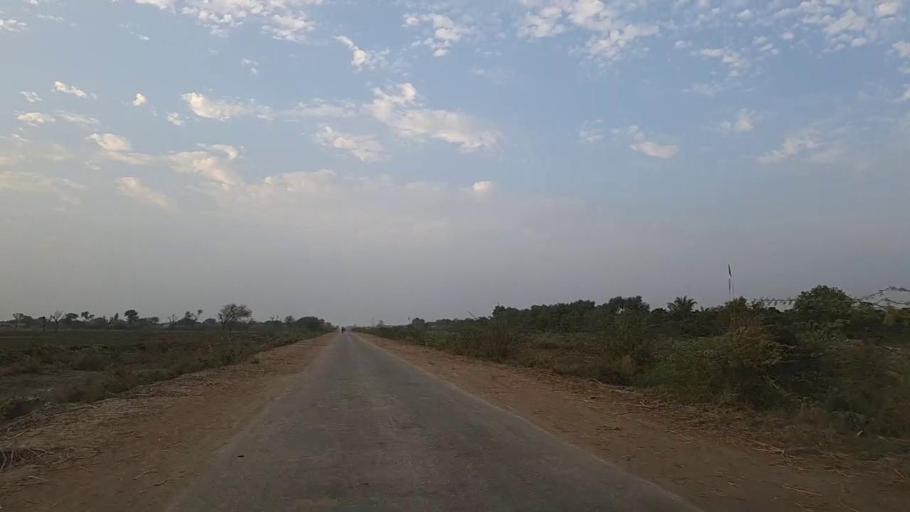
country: PK
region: Sindh
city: Mirwah Gorchani
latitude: 25.3221
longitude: 69.2187
